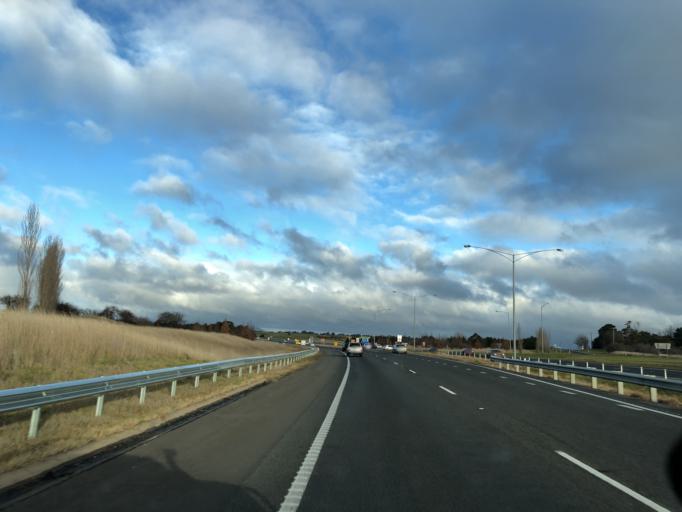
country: AU
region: Victoria
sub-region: Mount Alexander
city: Castlemaine
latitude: -37.2183
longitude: 144.4157
